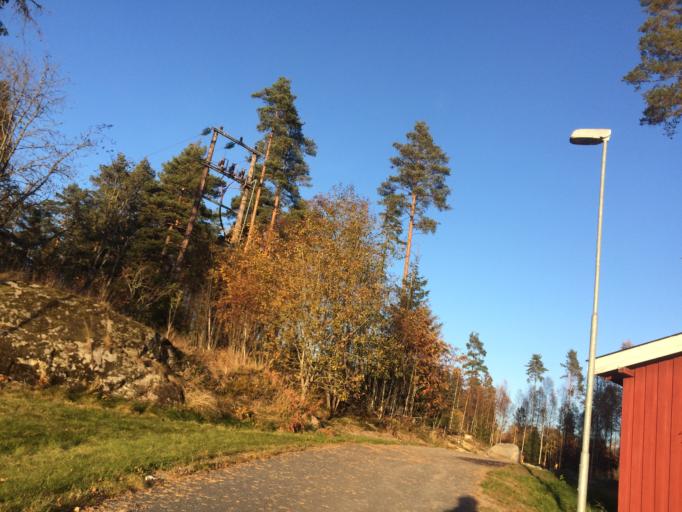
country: NO
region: Akershus
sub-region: Ski
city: Ski
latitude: 59.7259
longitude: 10.8637
